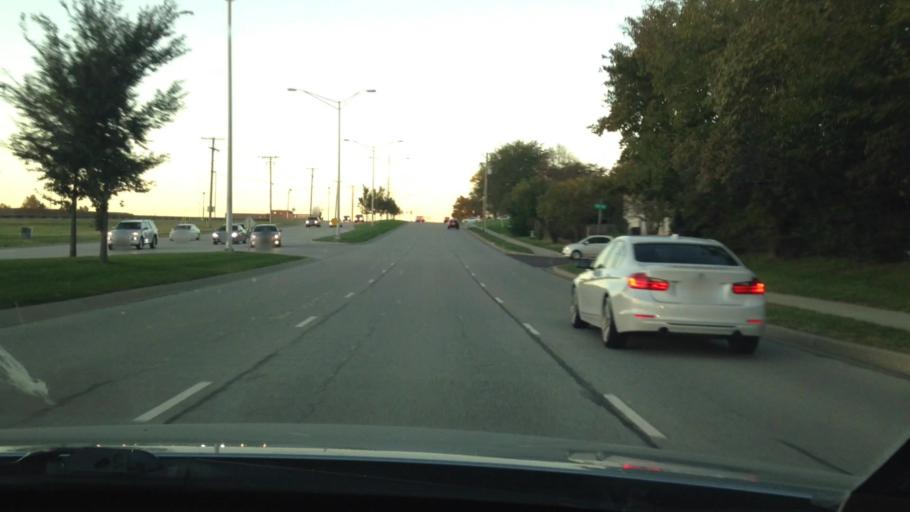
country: US
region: Kansas
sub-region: Johnson County
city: Lenexa
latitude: 38.9240
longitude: -94.7235
